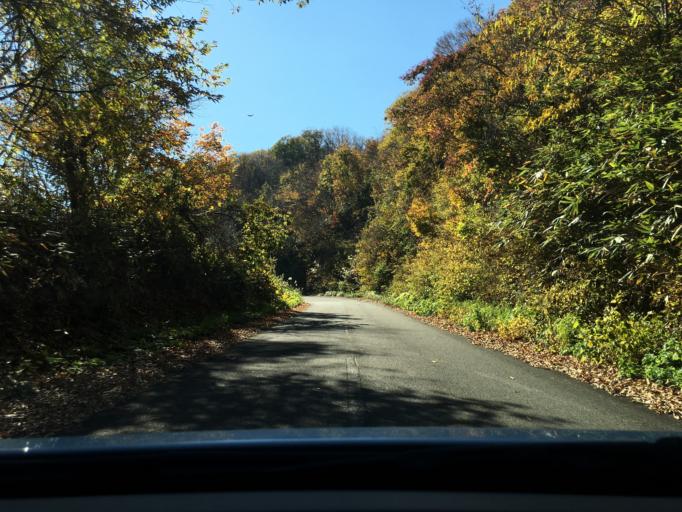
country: JP
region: Fukushima
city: Inawashiro
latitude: 37.4048
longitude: 140.0235
